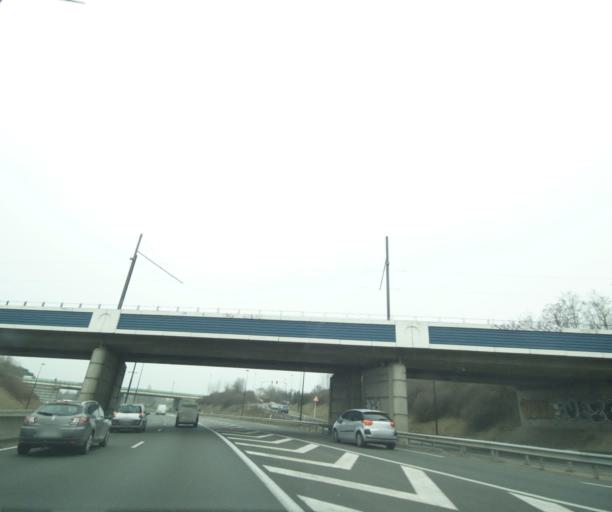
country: FR
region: Rhone-Alpes
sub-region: Departement du Rhone
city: Decines-Charpieu
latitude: 45.7730
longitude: 4.9847
